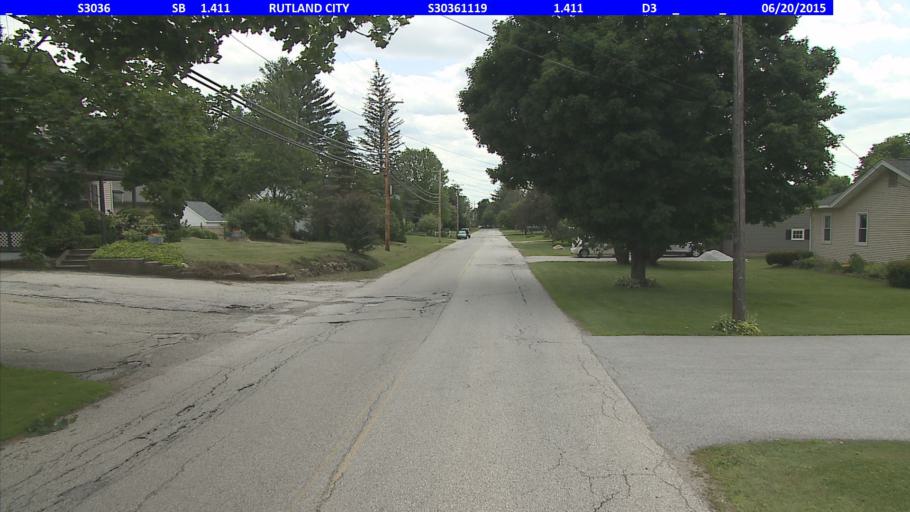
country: US
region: Vermont
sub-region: Rutland County
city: Rutland
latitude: 43.6286
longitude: -72.9788
